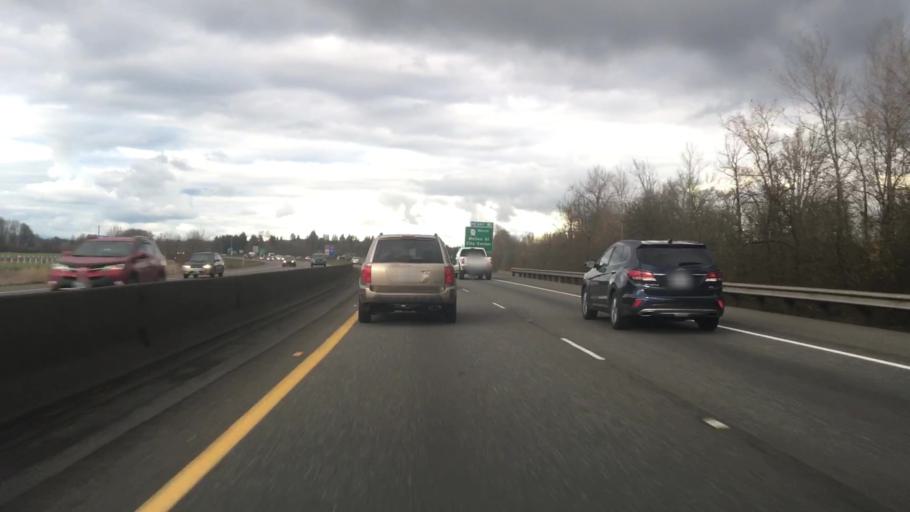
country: US
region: Washington
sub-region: Lewis County
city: Centralia
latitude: 46.6928
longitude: -122.9697
